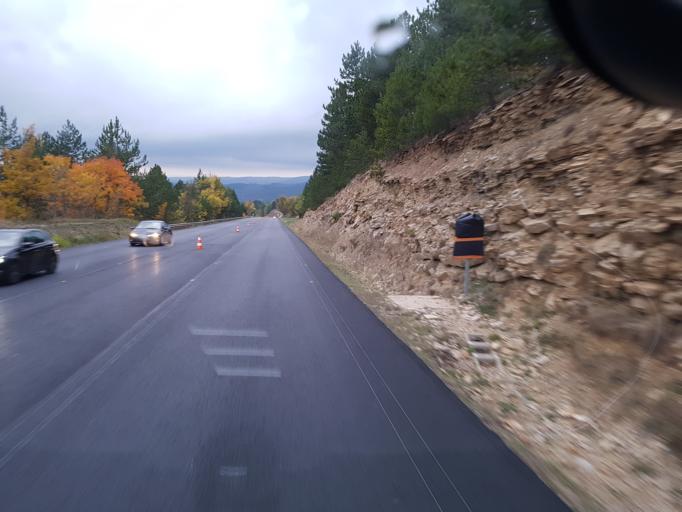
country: FR
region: Languedoc-Roussillon
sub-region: Departement de la Lozere
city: Mende
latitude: 44.5354
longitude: 3.5996
